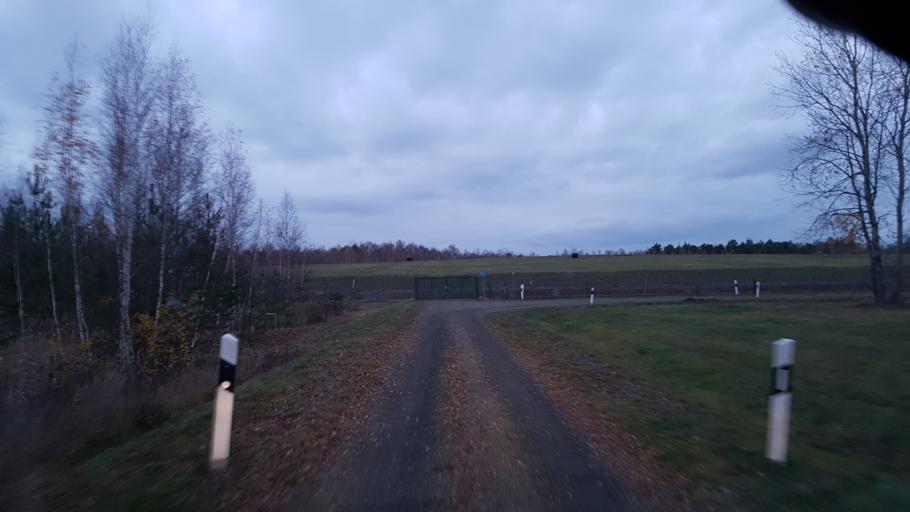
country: DE
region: Brandenburg
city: Lauchhammer
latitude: 51.4879
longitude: 13.7175
